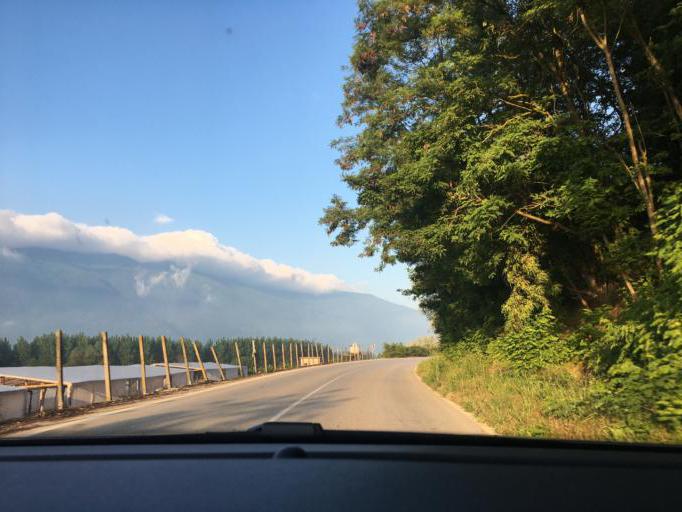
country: MK
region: Novo Selo
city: Novo Selo
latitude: 41.3977
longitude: 22.9807
